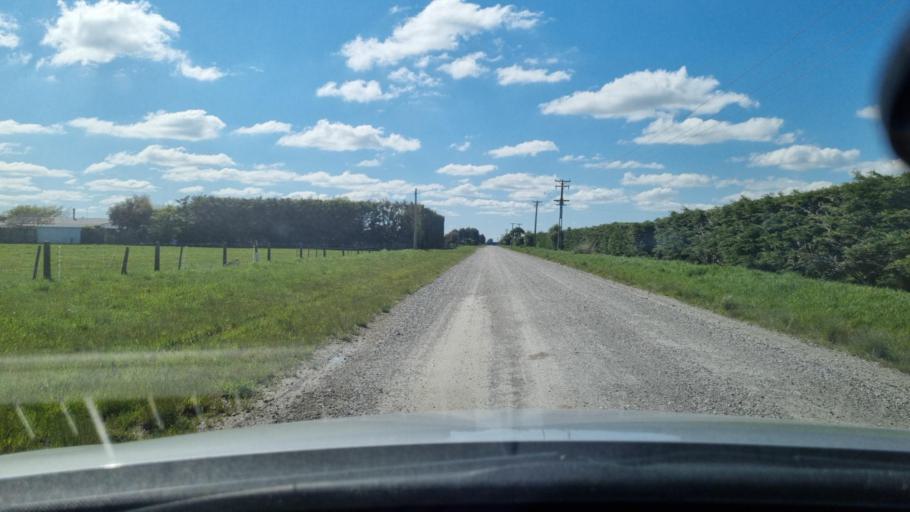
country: NZ
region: Southland
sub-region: Invercargill City
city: Invercargill
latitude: -46.3768
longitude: 168.2988
